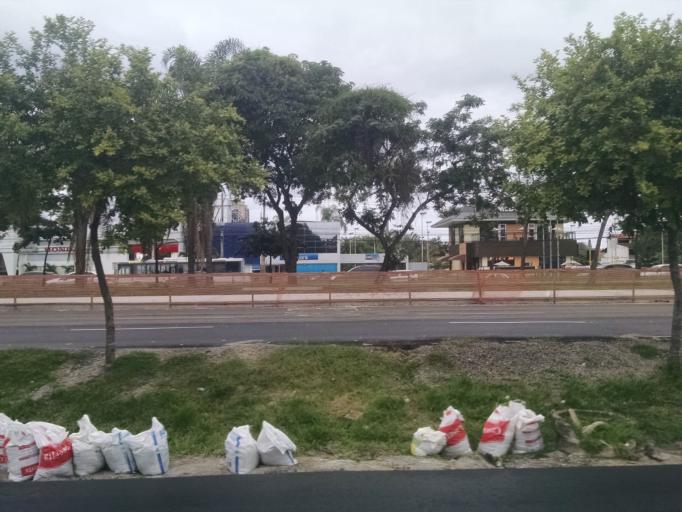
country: BR
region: Rio de Janeiro
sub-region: Rio De Janeiro
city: Rio de Janeiro
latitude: -23.0004
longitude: -43.3333
